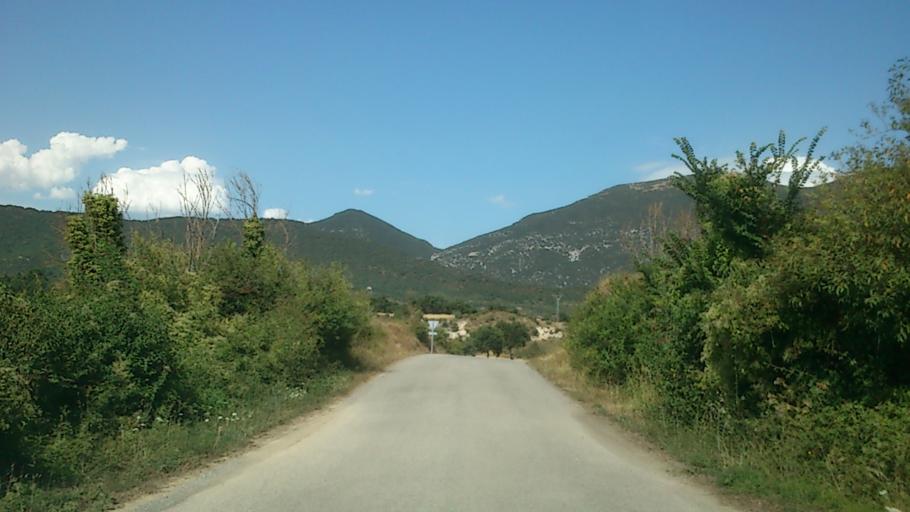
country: ES
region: Castille and Leon
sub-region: Provincia de Burgos
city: Frias
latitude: 42.8150
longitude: -3.2469
